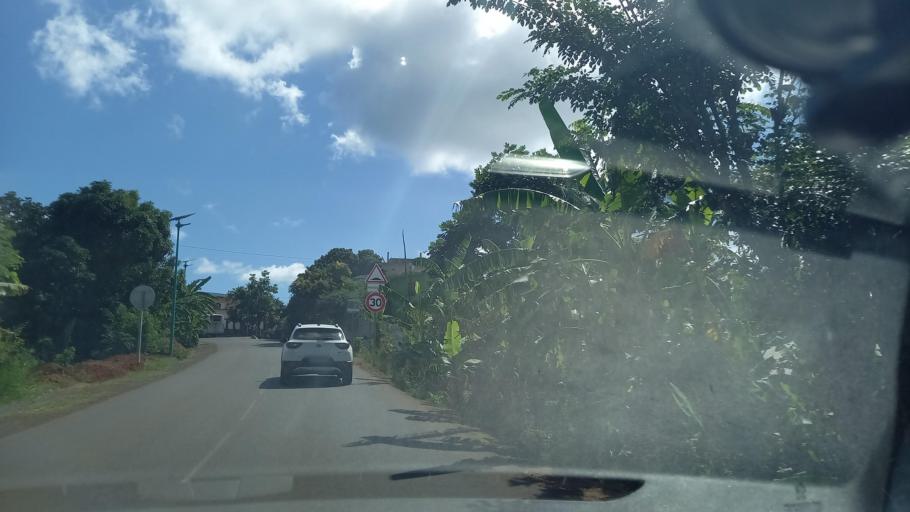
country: YT
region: Chirongui
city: Chirongui
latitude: -12.9064
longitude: 45.1567
